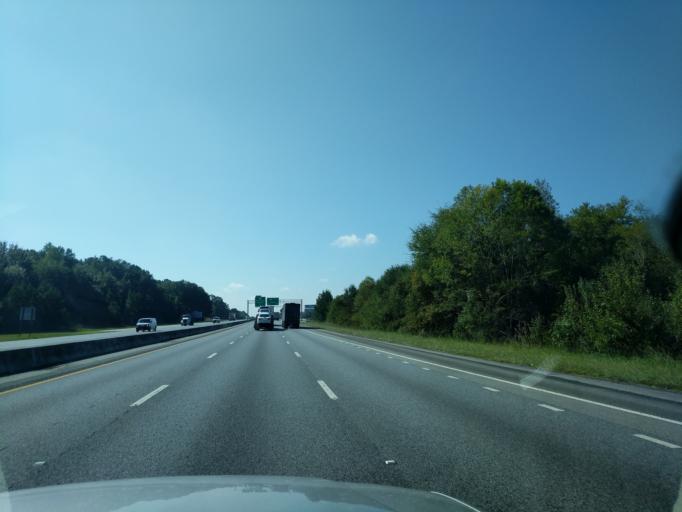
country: US
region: South Carolina
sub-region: Anderson County
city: Piedmont
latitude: 34.7102
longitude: -82.4997
